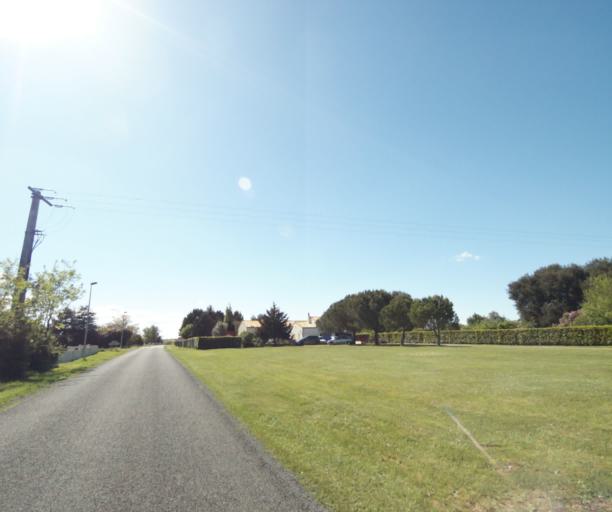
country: FR
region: Poitou-Charentes
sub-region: Departement de la Charente-Maritime
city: Bussac-sur-Charente
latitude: 45.8117
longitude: -0.6245
